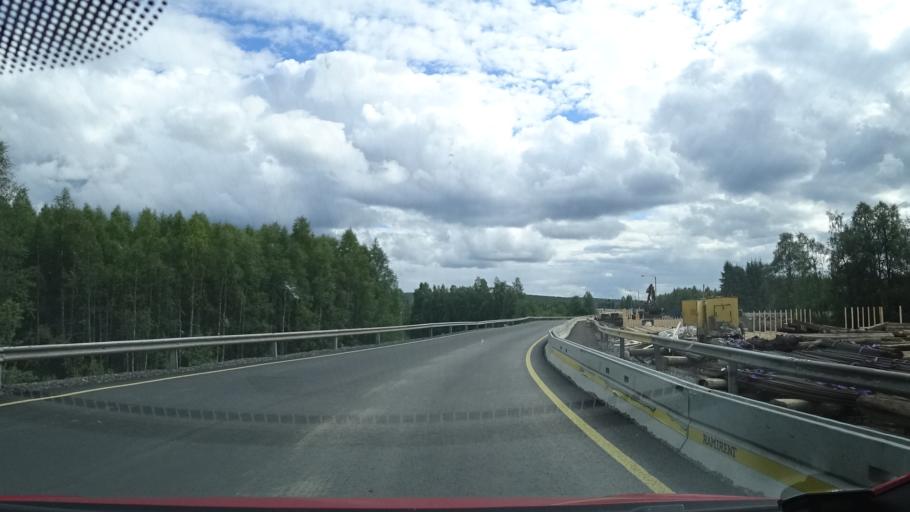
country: FI
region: Lapland
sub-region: Rovaniemi
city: Rovaniemi
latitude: 66.5241
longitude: 25.7450
